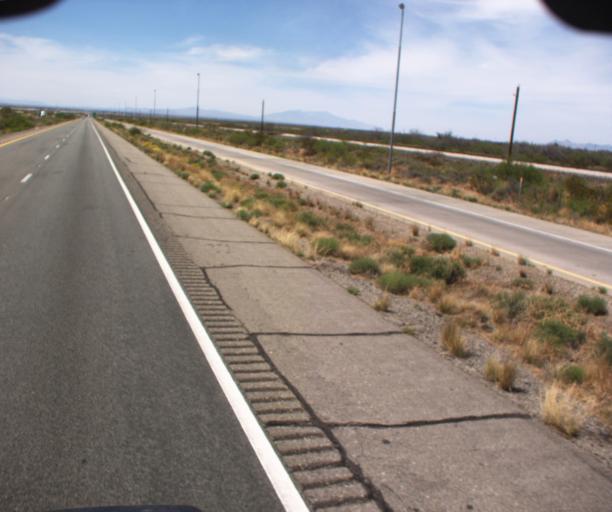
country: US
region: New Mexico
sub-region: Hidalgo County
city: Lordsburg
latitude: 32.2543
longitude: -109.1641
